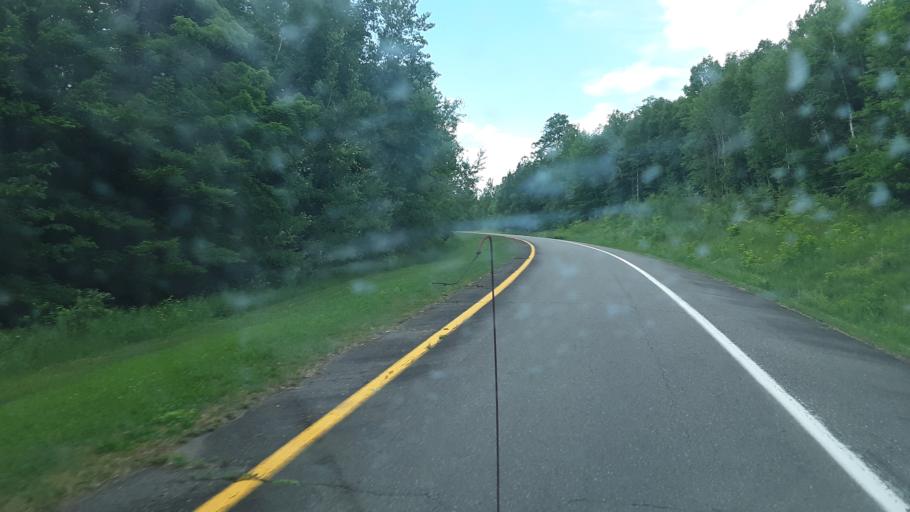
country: US
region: Maine
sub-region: Penobscot County
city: Medway
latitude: 45.7110
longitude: -68.4743
